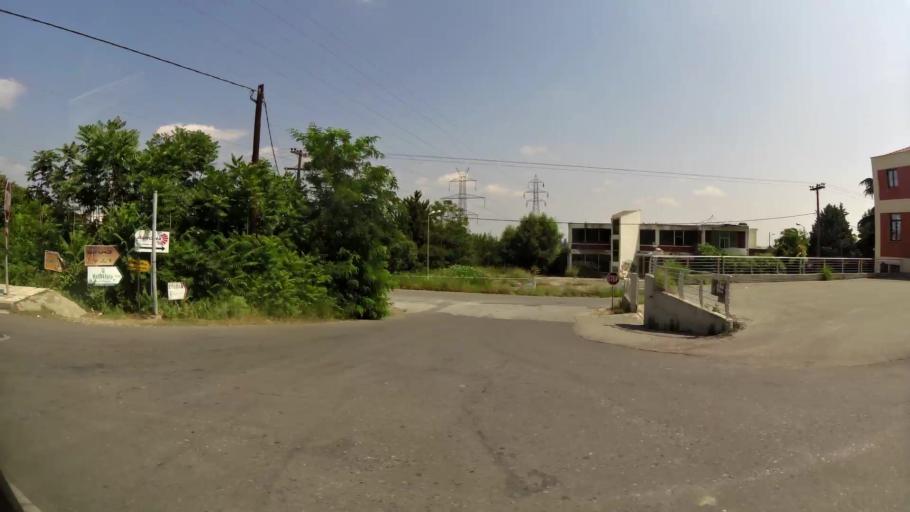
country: GR
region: Central Macedonia
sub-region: Nomos Imathias
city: Veroia
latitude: 40.5090
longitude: 22.2207
